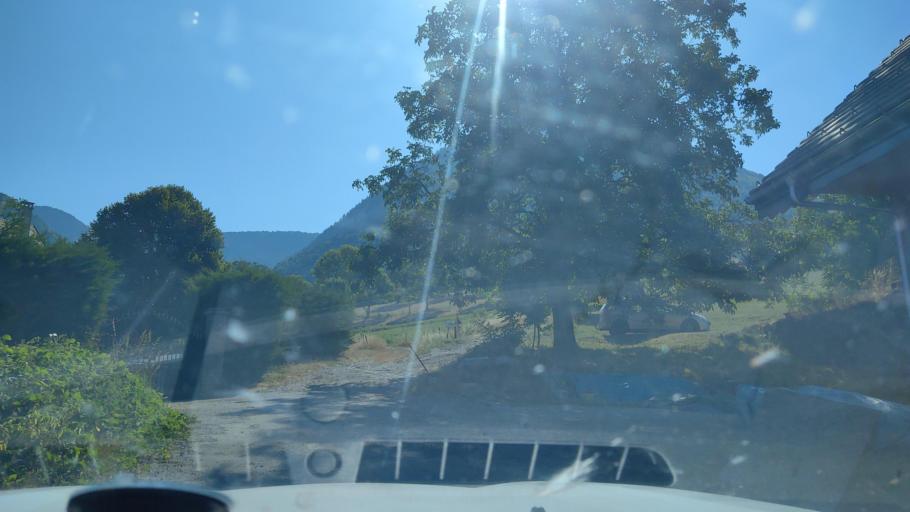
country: FR
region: Rhone-Alpes
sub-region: Departement de la Savoie
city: Barby
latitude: 45.5738
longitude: 6.0366
